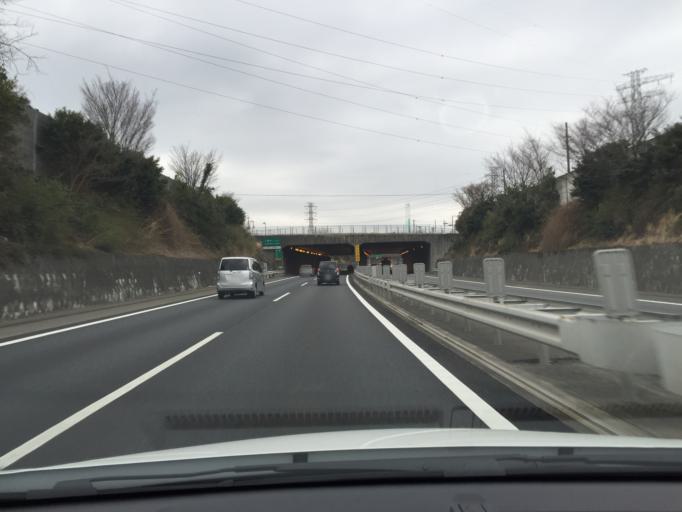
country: JP
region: Saitama
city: Sayama
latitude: 35.8232
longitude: 139.3731
